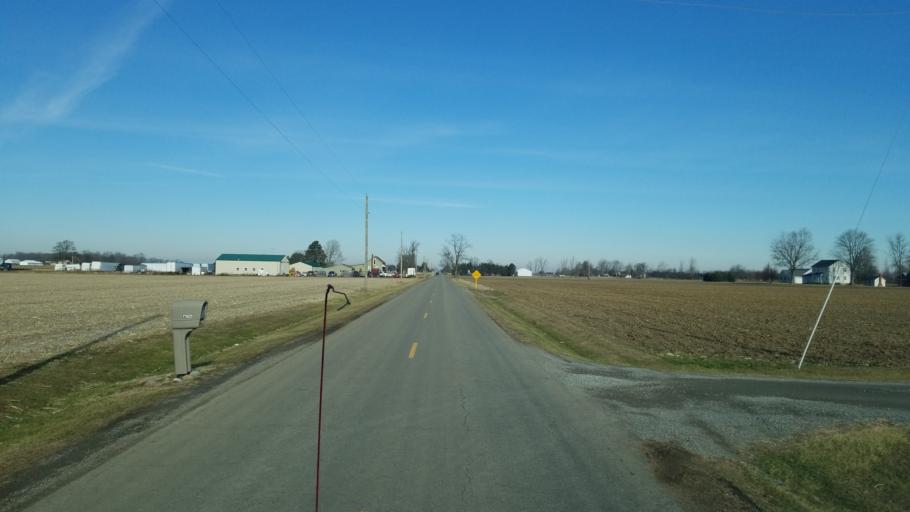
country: US
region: Ohio
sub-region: Putnam County
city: Pandora
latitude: 40.9246
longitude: -83.9378
